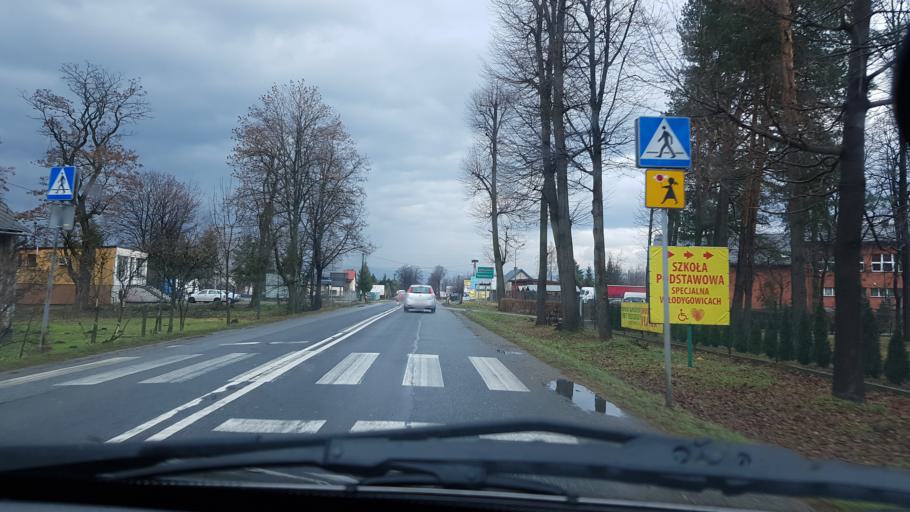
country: PL
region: Silesian Voivodeship
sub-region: Powiat zywiecki
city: Zarzecze
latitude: 49.7158
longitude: 19.1572
